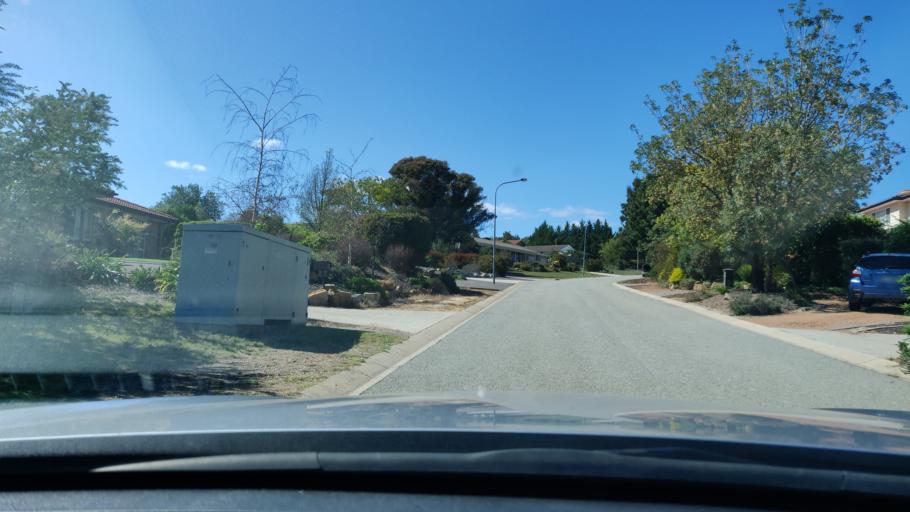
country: AU
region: Australian Capital Territory
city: Macarthur
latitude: -35.4403
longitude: 149.1005
